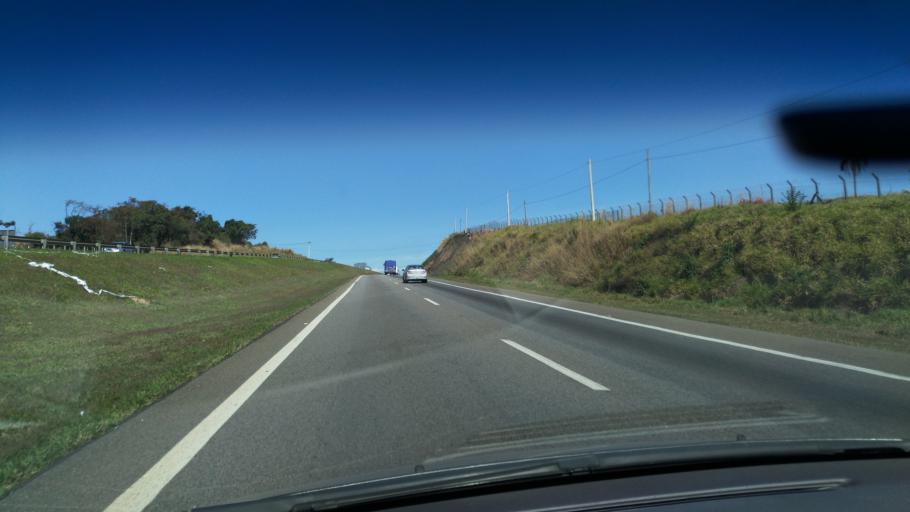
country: BR
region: Sao Paulo
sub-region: Jaguariuna
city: Jaguariuna
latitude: -22.6685
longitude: -47.0029
